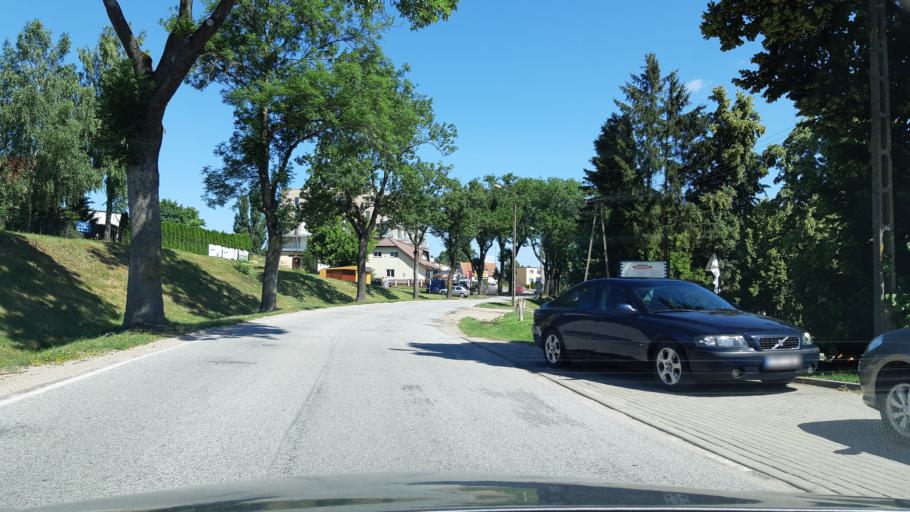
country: PL
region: Warmian-Masurian Voivodeship
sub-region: Powiat gizycki
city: Gizycko
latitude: 54.0099
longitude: 21.7354
